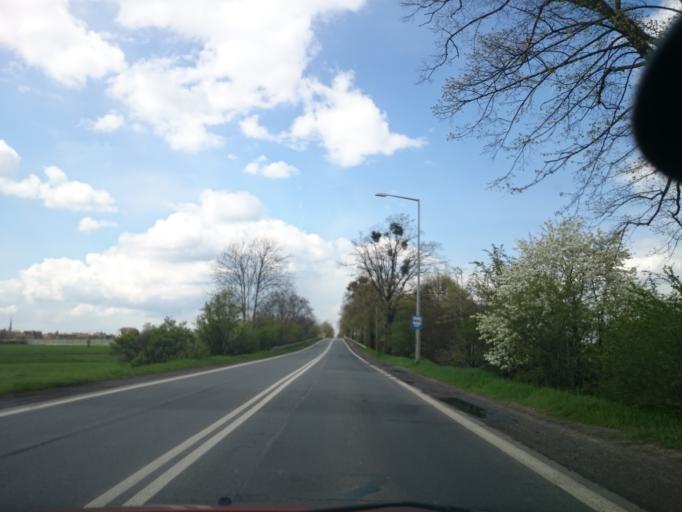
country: PL
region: Opole Voivodeship
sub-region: Powiat opolski
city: Opole
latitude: 50.6507
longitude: 17.9694
